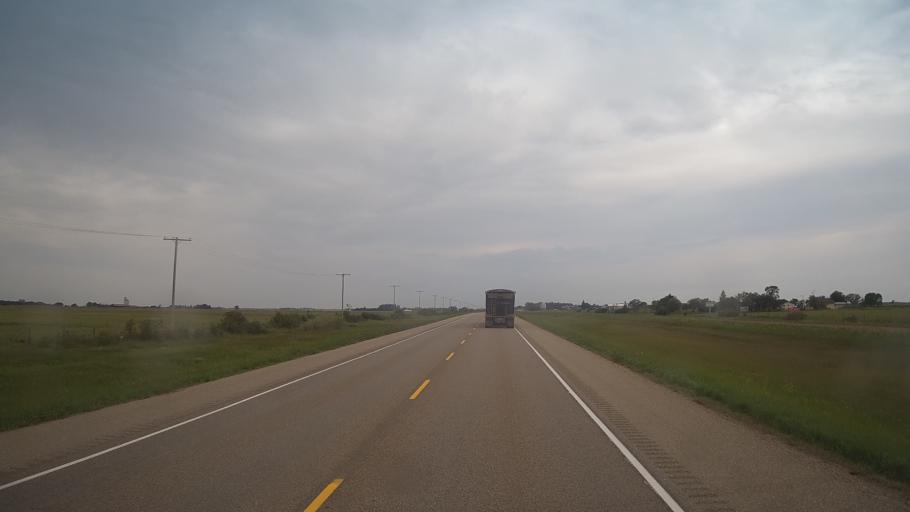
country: CA
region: Saskatchewan
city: Langham
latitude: 52.1289
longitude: -107.1869
